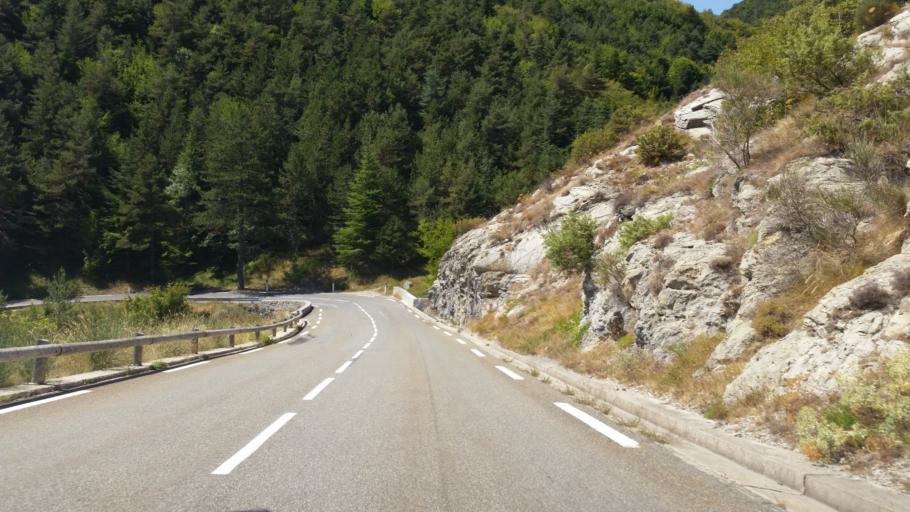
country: FR
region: Provence-Alpes-Cote d'Azur
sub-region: Departement des Alpes-Maritimes
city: Breil-sur-Roya
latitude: 43.9216
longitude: 7.4727
